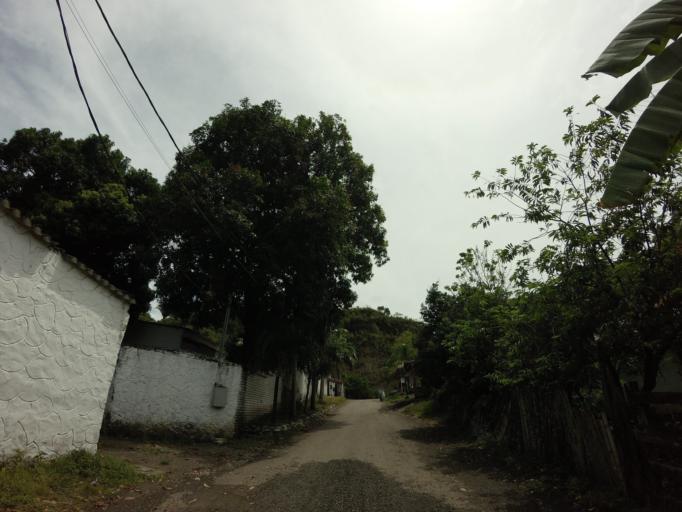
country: CO
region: Caldas
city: La Dorada
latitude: 5.4112
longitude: -74.6890
